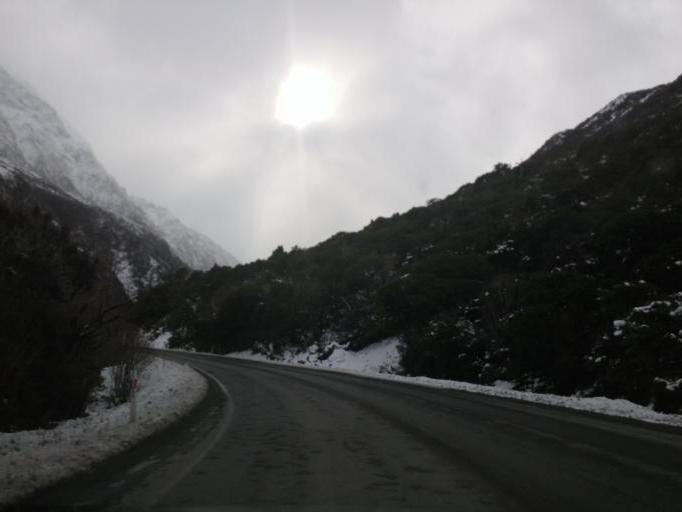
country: NZ
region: West Coast
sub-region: Grey District
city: Greymouth
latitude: -42.8943
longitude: 171.5592
